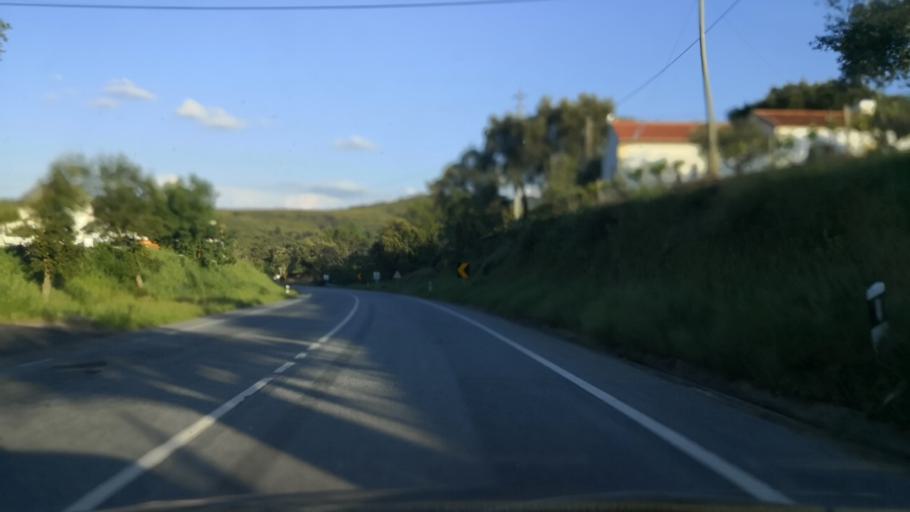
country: PT
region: Portalegre
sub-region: Portalegre
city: Sao Juliao
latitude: 39.3648
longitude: -7.3350
